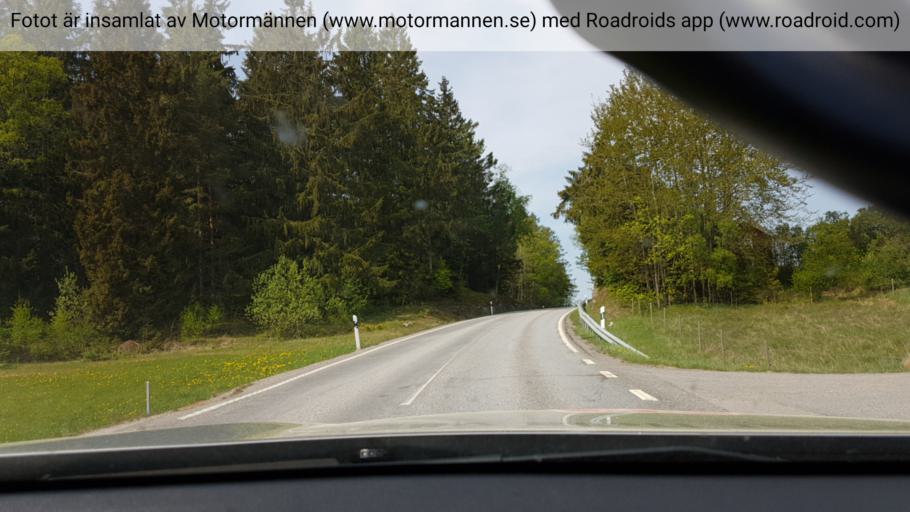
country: SE
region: Stockholm
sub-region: Nynashamns Kommun
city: Osmo
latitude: 58.9871
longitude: 17.8219
